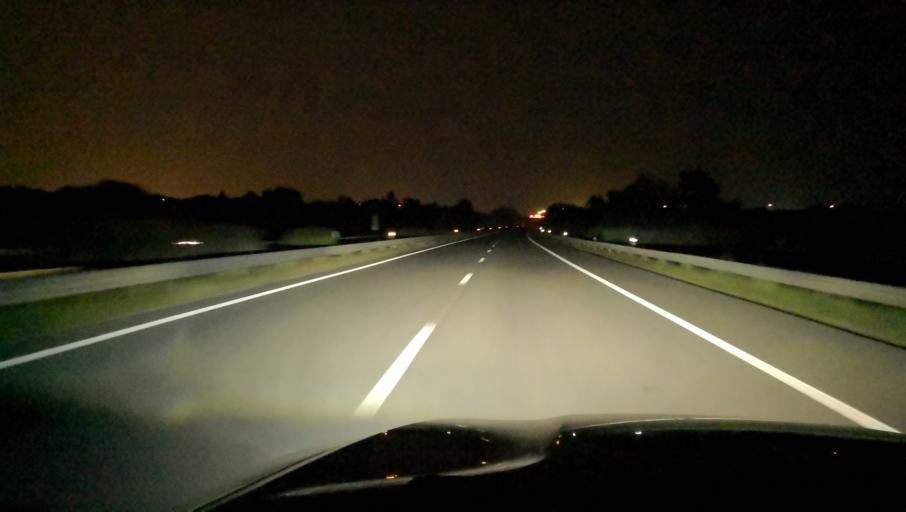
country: PT
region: Setubal
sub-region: Setubal
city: Setubal
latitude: 38.5480
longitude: -8.8714
